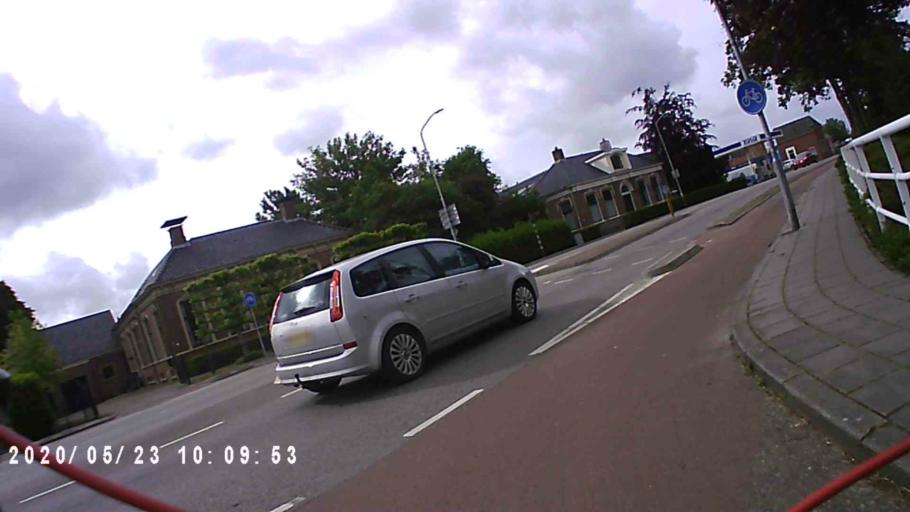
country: NL
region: Groningen
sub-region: Gemeente Appingedam
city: Appingedam
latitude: 53.3201
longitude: 6.8620
